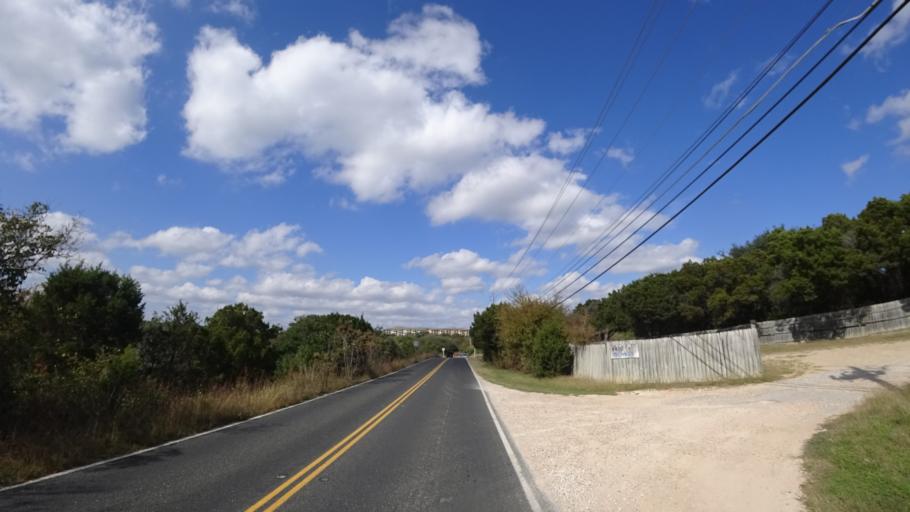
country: US
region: Texas
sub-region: Travis County
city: Barton Creek
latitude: 30.2539
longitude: -97.8886
